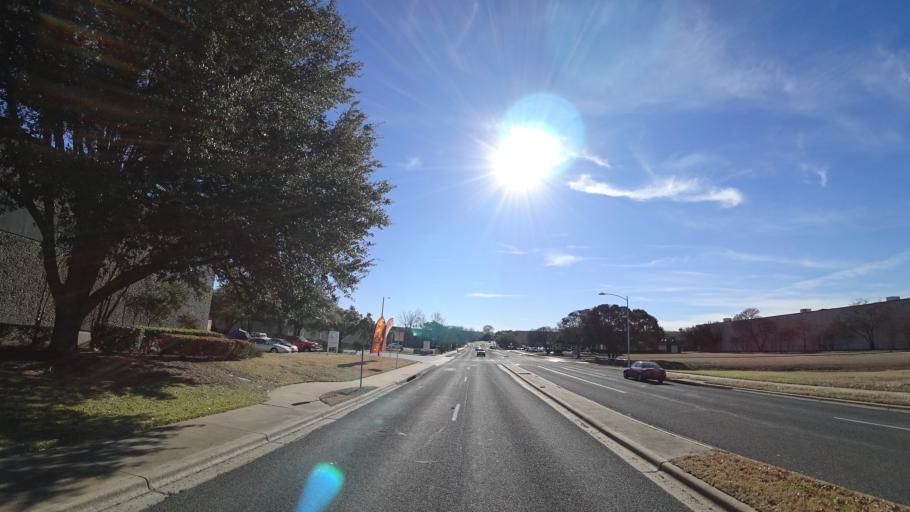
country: US
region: Texas
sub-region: Travis County
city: Wells Branch
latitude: 30.3843
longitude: -97.7130
